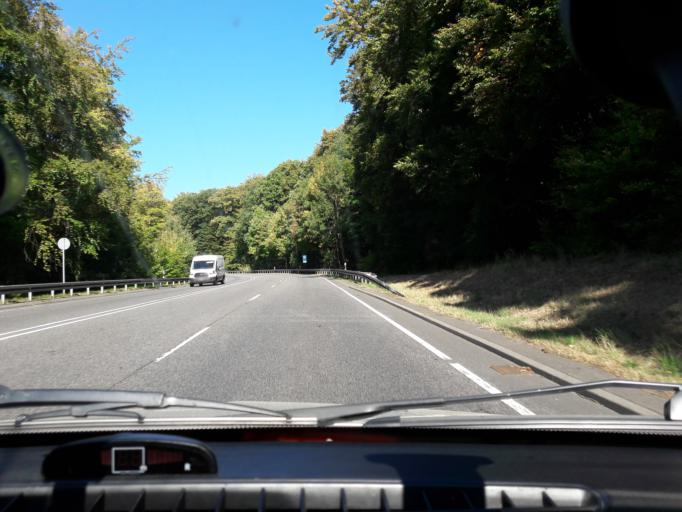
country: DE
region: Hesse
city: Taunusstein
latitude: 50.1213
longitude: 8.1754
